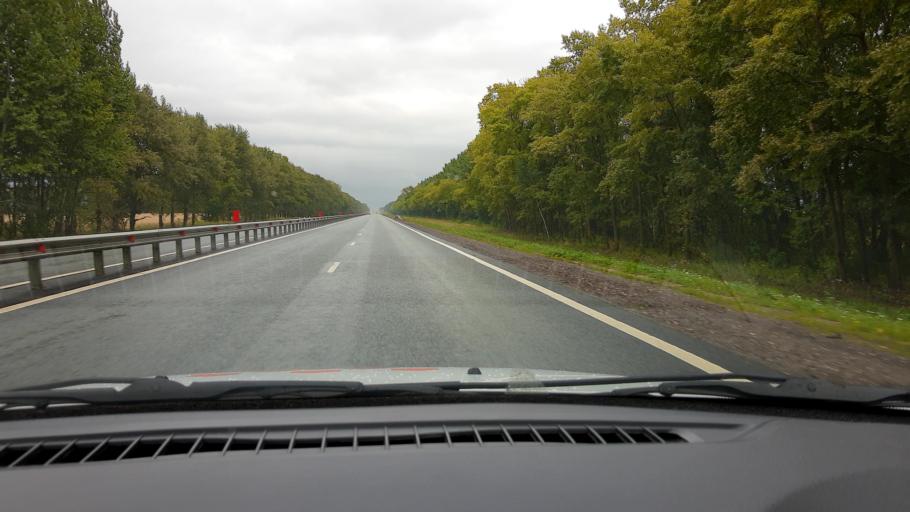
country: RU
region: Chuvashia
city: Yantikovo
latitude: 55.7900
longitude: 47.7587
